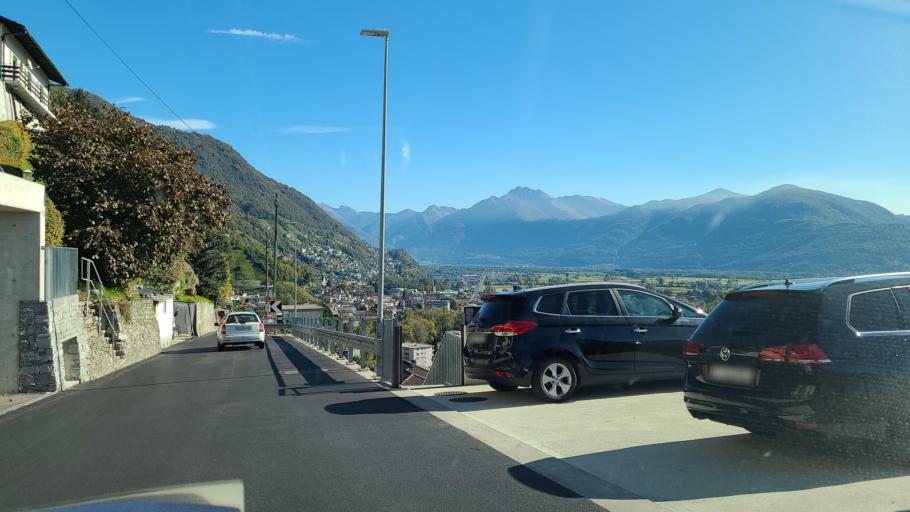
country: CH
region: Ticino
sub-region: Locarno District
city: Gordola
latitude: 46.1823
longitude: 8.8461
